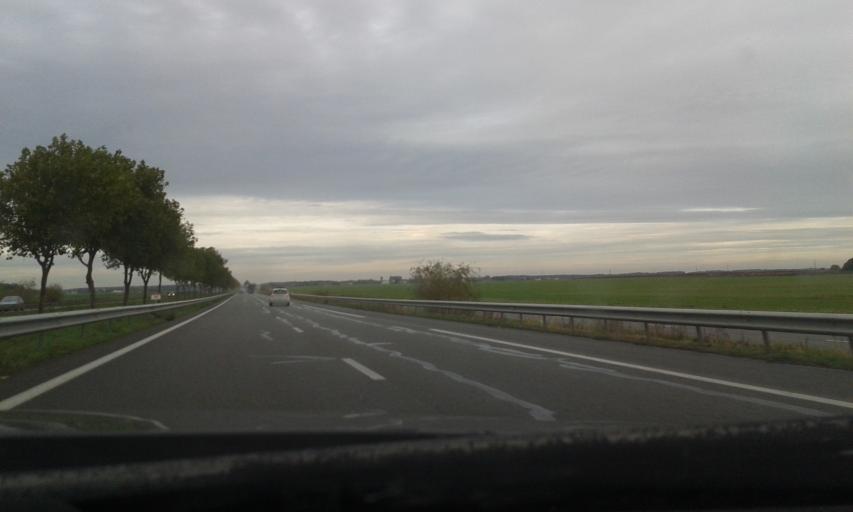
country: FR
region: Centre
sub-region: Departement d'Eure-et-Loir
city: Luray
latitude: 48.6579
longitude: 1.3955
